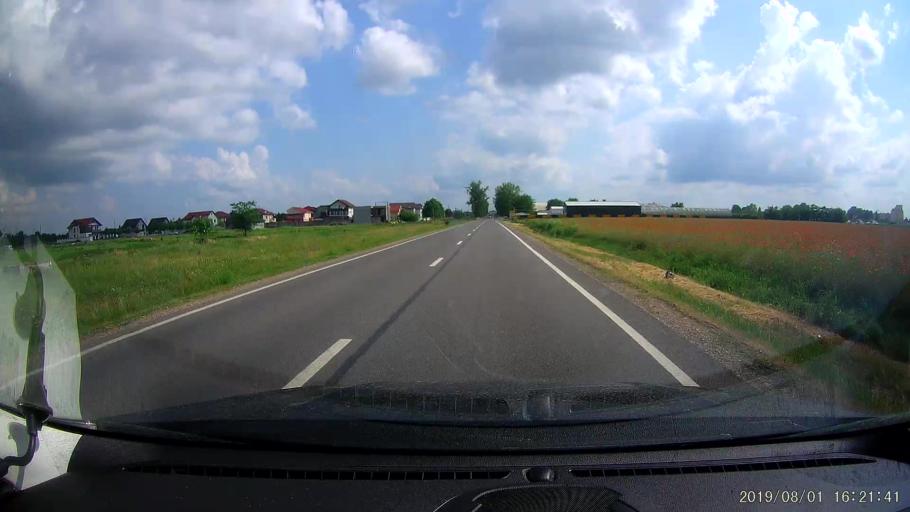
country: RO
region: Calarasi
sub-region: Municipiul Calarasi
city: Calarasi
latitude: 44.2134
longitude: 27.3393
